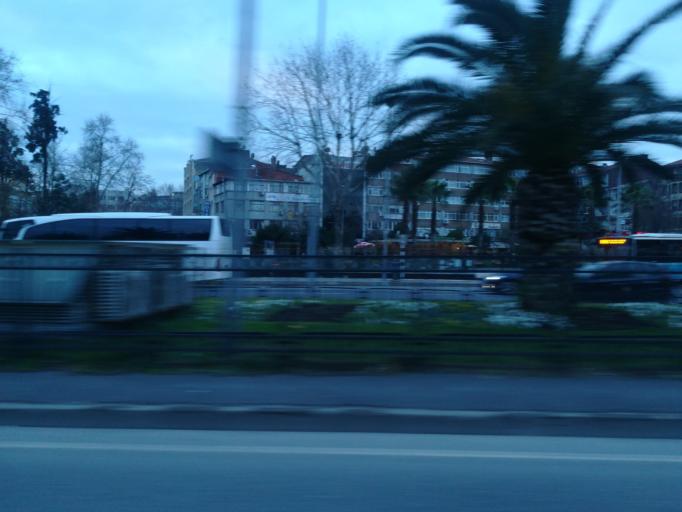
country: TR
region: Istanbul
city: Istanbul
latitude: 41.0112
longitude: 28.9488
